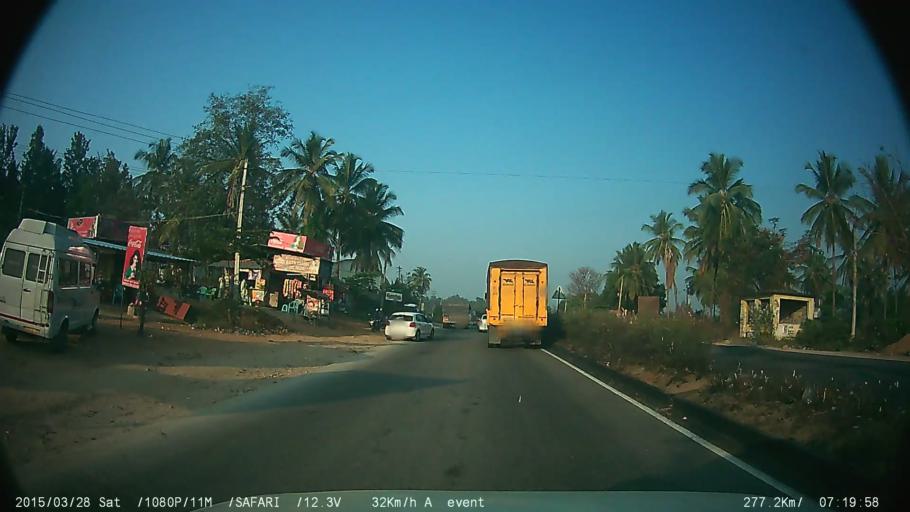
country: IN
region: Karnataka
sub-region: Mandya
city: Mandya
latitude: 12.4984
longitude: 76.8151
